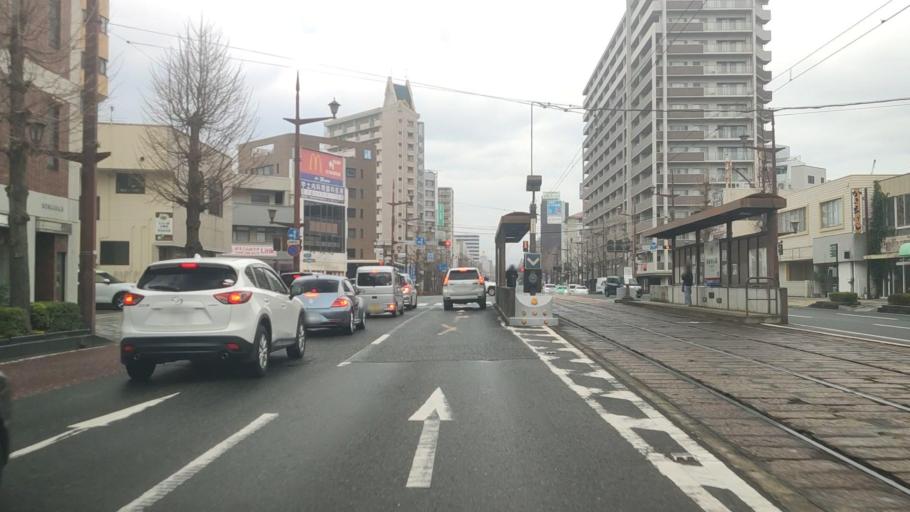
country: JP
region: Kumamoto
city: Kumamoto
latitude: 32.7894
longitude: 130.7331
